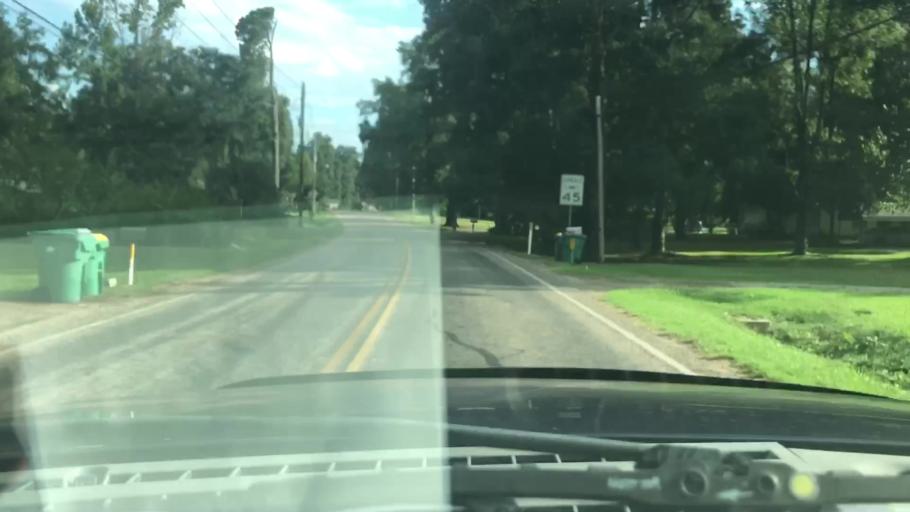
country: US
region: Texas
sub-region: Bowie County
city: Texarkana
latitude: 33.4023
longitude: -94.0649
